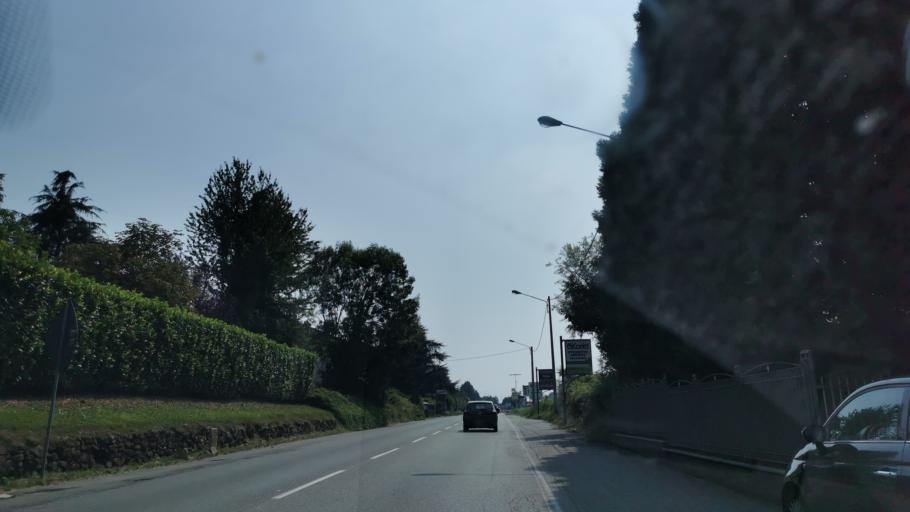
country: IT
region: Lombardy
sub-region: Provincia di Lecco
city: Calco
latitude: 45.7206
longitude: 9.4117
